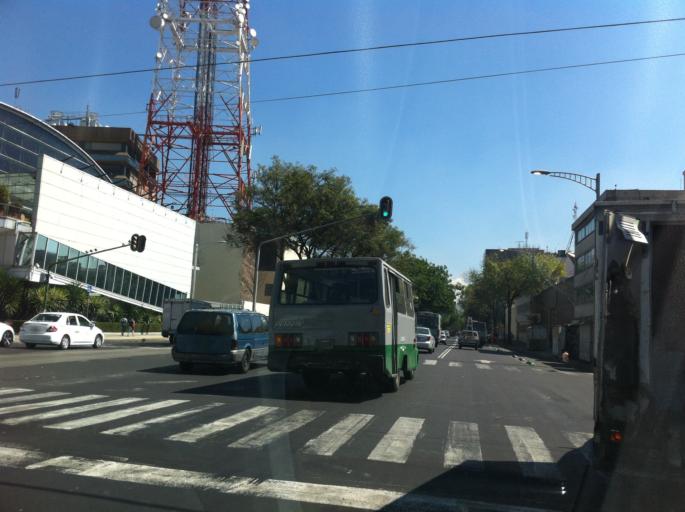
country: MX
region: Mexico City
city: Cuauhtemoc
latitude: 19.4256
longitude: -99.1513
